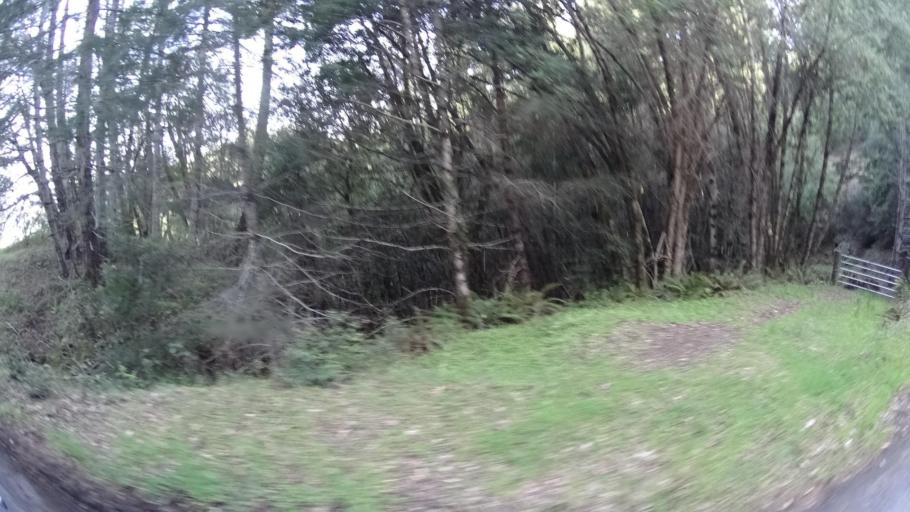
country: US
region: California
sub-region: Humboldt County
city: Hydesville
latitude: 40.6725
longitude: -123.9306
